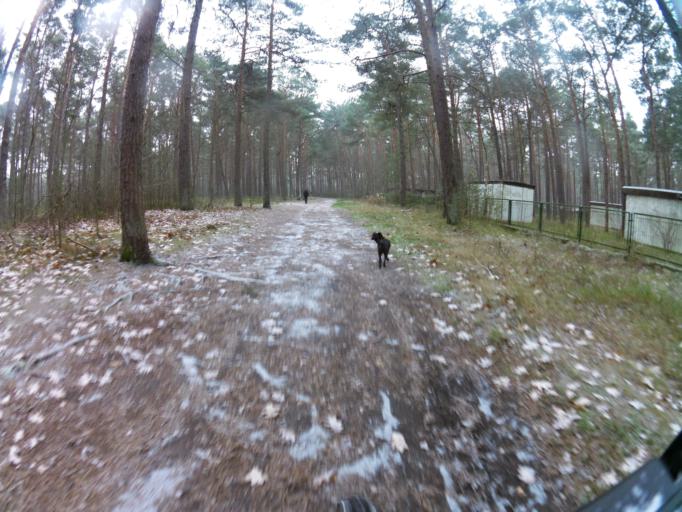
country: PL
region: West Pomeranian Voivodeship
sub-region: Powiat gryficki
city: Cerkwica
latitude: 54.1047
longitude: 15.1313
